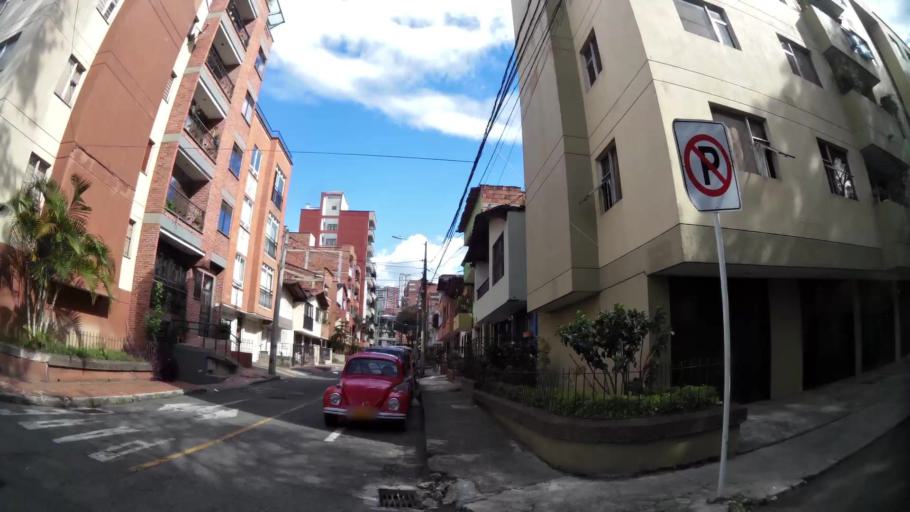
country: CO
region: Antioquia
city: Sabaneta
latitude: 6.1532
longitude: -75.6194
